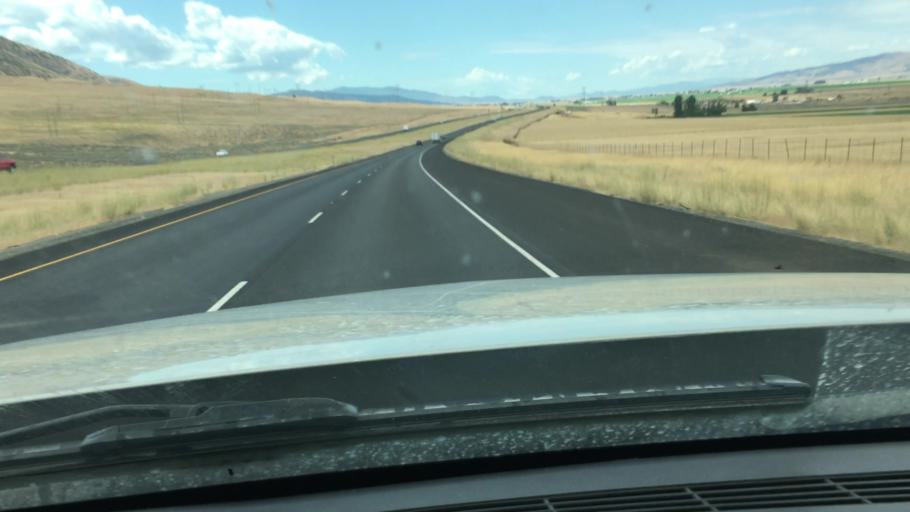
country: US
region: Utah
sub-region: Juab County
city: Mona
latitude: 39.7844
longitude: -111.8377
